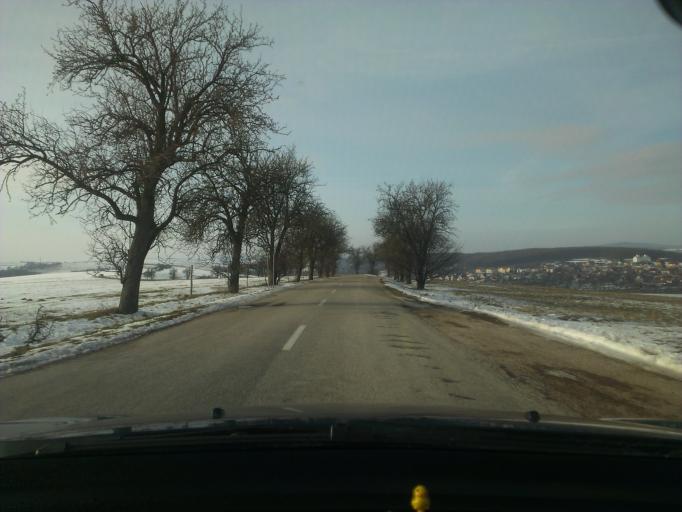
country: SK
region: Nitriansky
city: Stara Tura
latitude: 48.7477
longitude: 17.6399
